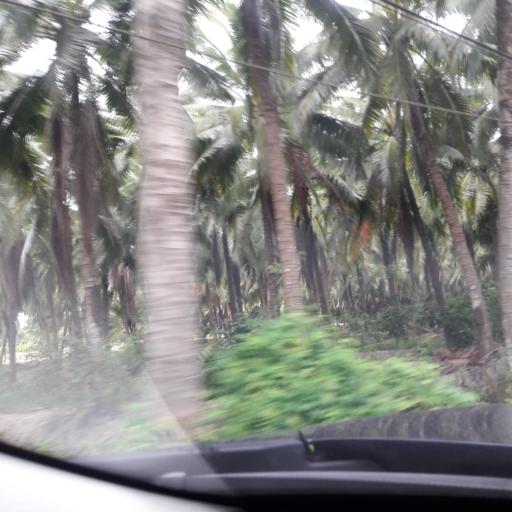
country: TH
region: Ratchaburi
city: Damnoen Saduak
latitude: 13.5713
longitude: 99.9489
